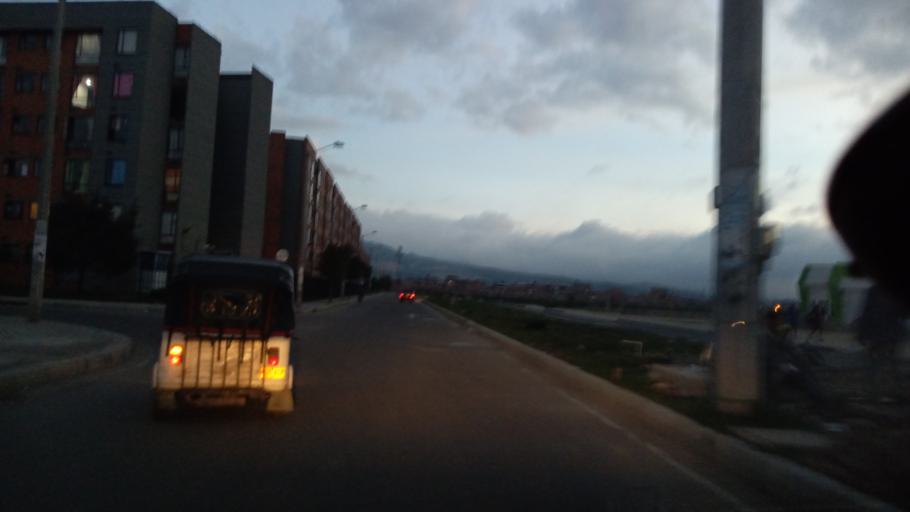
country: CO
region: Cundinamarca
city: Soacha
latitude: 4.5789
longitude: -74.2341
